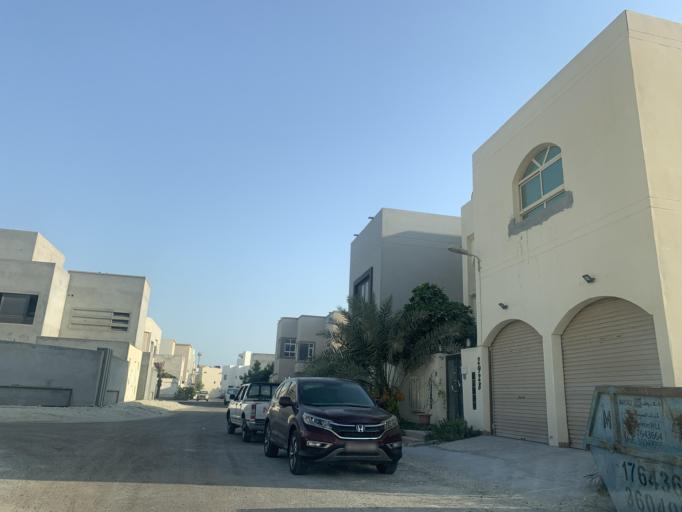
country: BH
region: Muharraq
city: Al Muharraq
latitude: 26.2880
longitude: 50.6297
